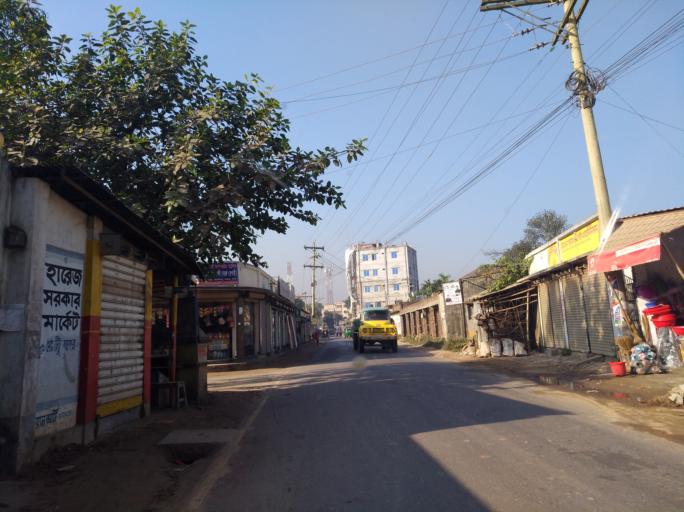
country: BD
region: Dhaka
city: Tungi
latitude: 23.9068
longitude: 90.2864
